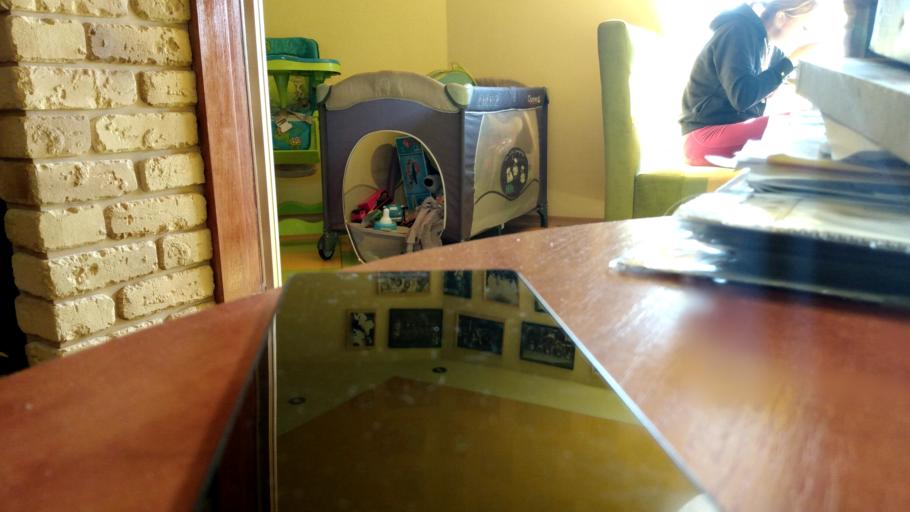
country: RU
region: Penza
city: Serdobsk
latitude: 52.4228
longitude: 44.3116
